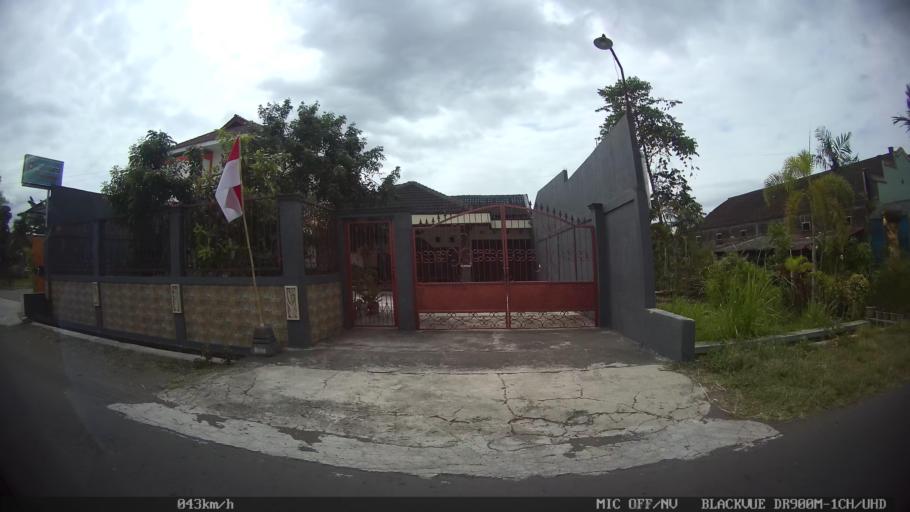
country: ID
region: Daerah Istimewa Yogyakarta
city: Depok
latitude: -7.8185
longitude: 110.4427
